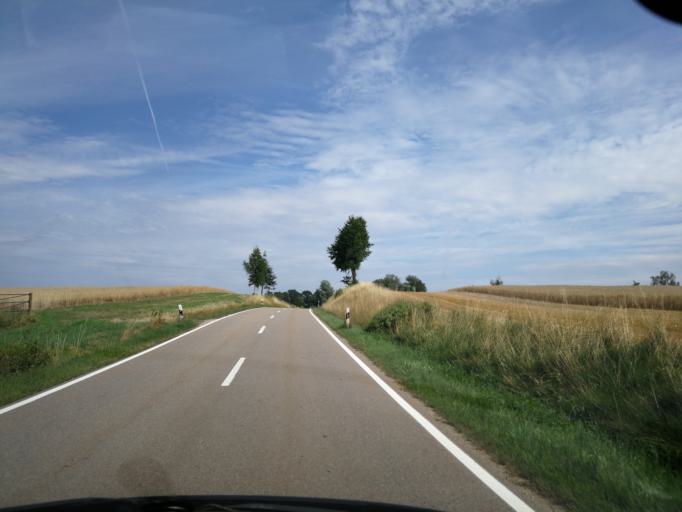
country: DE
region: Bavaria
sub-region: Lower Bavaria
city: Wiesenfelden
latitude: 49.0424
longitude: 12.5436
